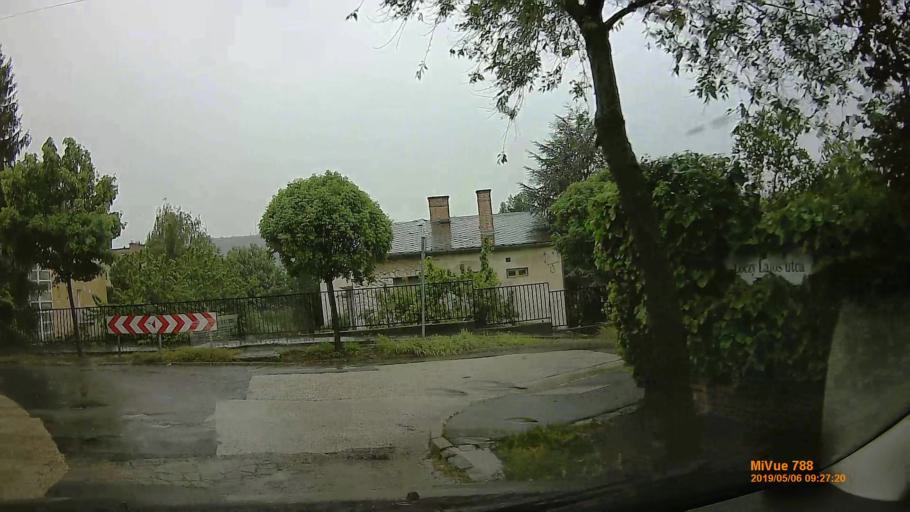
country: HU
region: Budapest
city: Budapest II. keruelet
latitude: 47.5174
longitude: 19.0084
